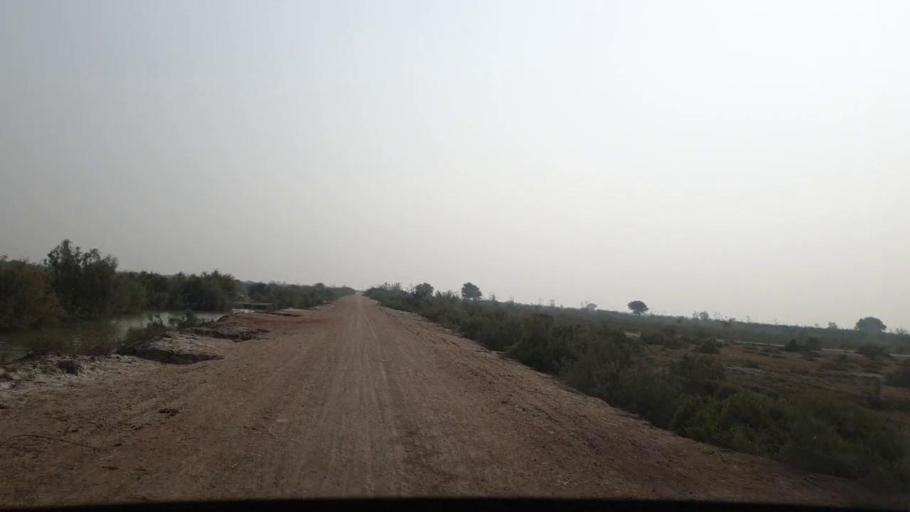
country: PK
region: Sindh
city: Jati
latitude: 24.2788
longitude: 68.4230
